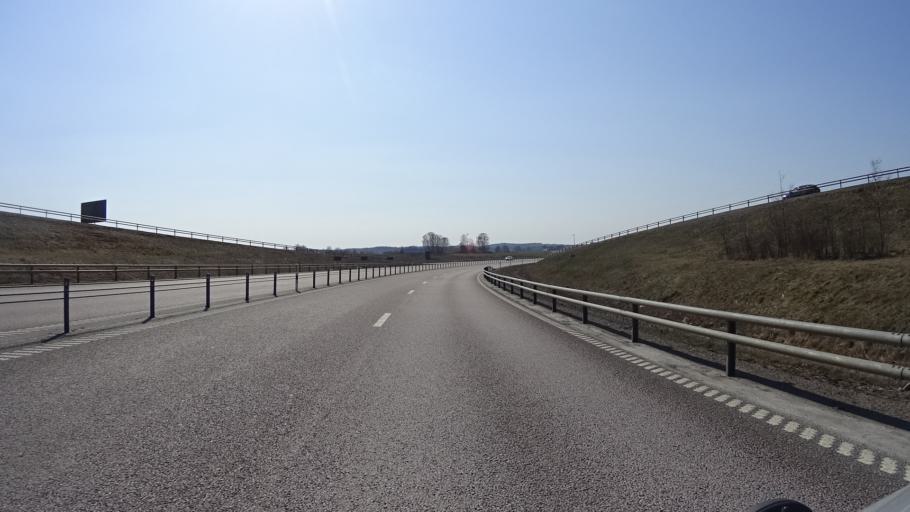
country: SE
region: OEstergoetland
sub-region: Mjolby Kommun
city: Mjolby
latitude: 58.3371
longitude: 15.1043
